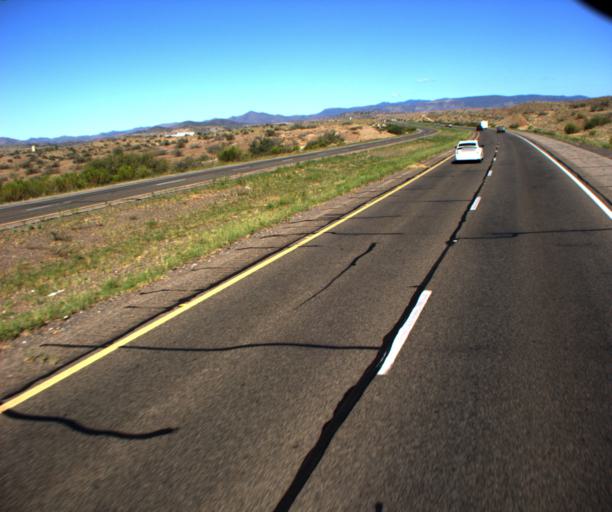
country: US
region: Arizona
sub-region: Yavapai County
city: Spring Valley
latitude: 34.3469
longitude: -112.1454
